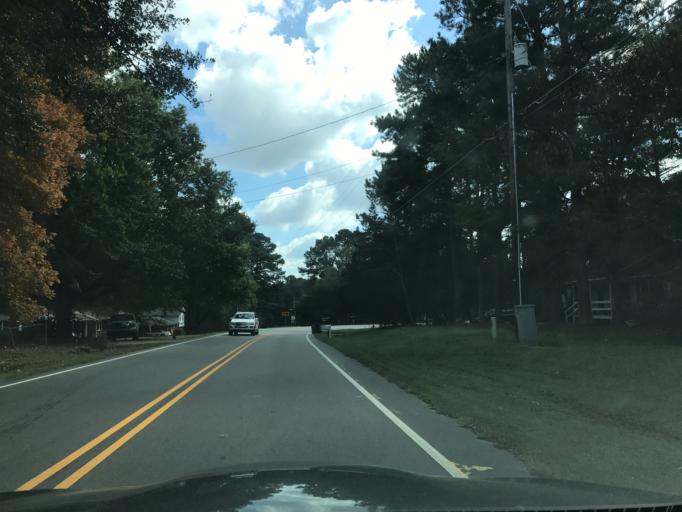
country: US
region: North Carolina
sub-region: Wake County
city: Wake Forest
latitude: 35.9474
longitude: -78.5299
